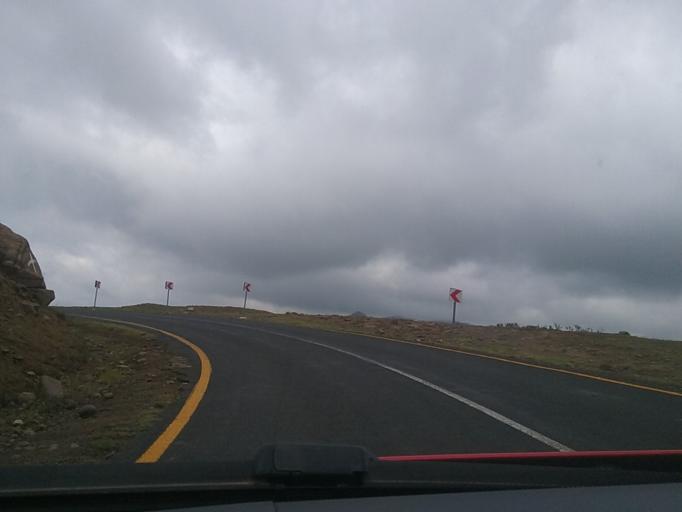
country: LS
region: Berea
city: Teyateyaneng
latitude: -29.2329
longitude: 27.8631
